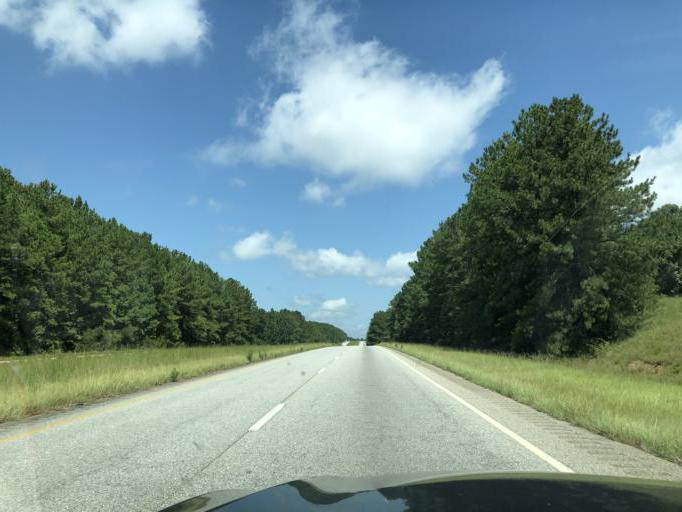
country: US
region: Alabama
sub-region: Henry County
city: Abbeville
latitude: 31.6765
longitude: -85.2793
